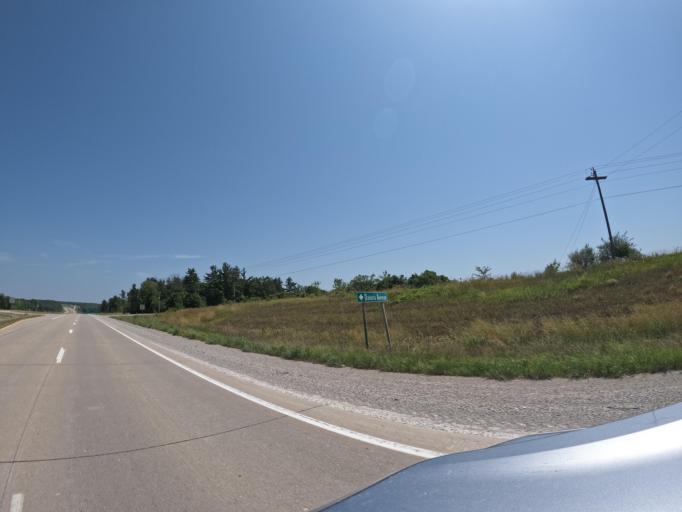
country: US
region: Iowa
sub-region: Henry County
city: Mount Pleasant
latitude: 40.9748
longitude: -91.6611
